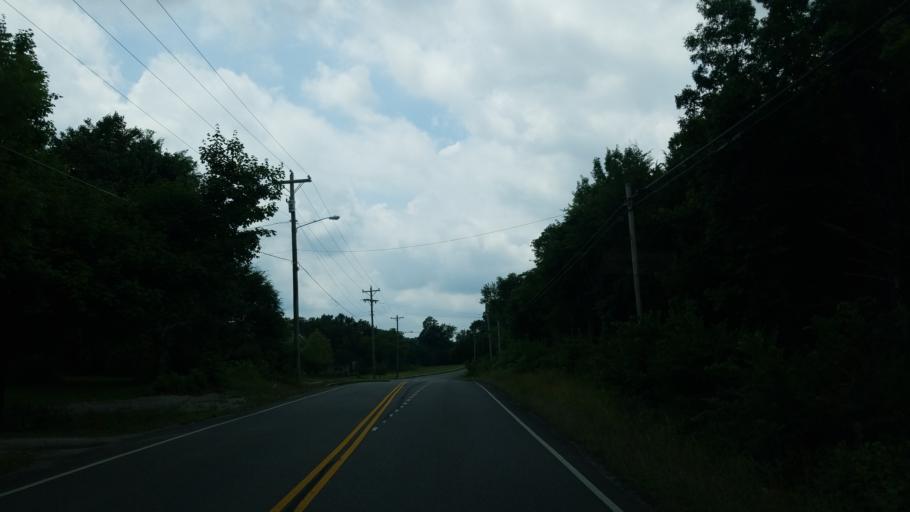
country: US
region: Tennessee
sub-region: Rutherford County
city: La Vergne
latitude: 36.0558
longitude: -86.5864
